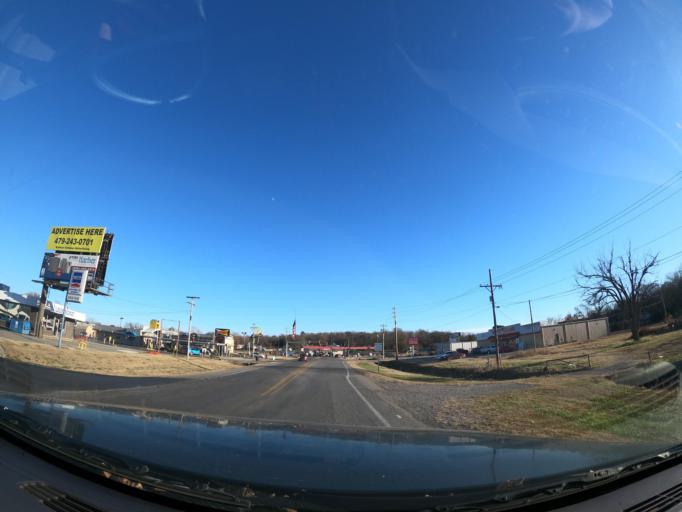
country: US
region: Oklahoma
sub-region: Latimer County
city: Wilburton
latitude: 34.9183
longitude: -95.3179
